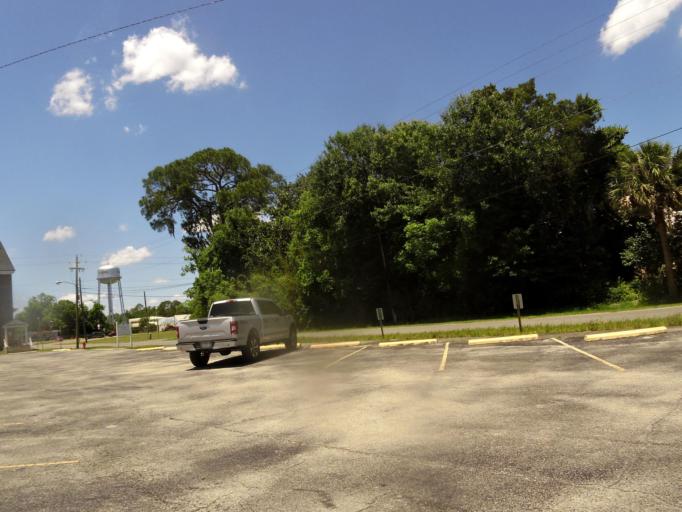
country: US
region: Florida
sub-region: Bradford County
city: Starke
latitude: 29.9454
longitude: -82.1095
